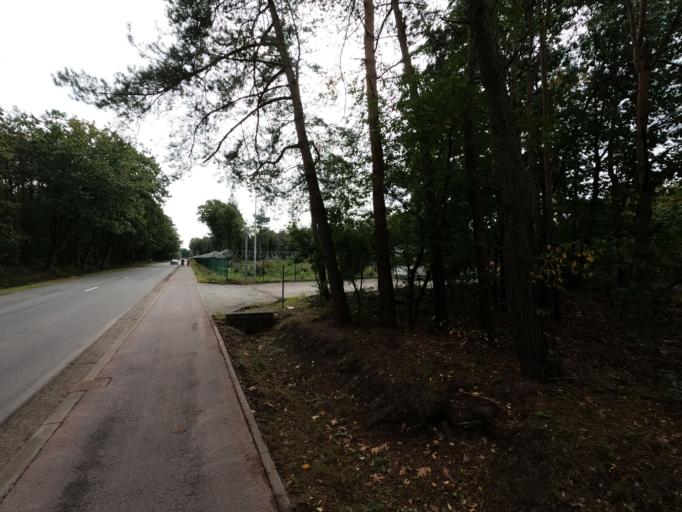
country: BE
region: Flanders
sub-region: Provincie Antwerpen
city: Dessel
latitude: 51.2303
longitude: 5.0906
